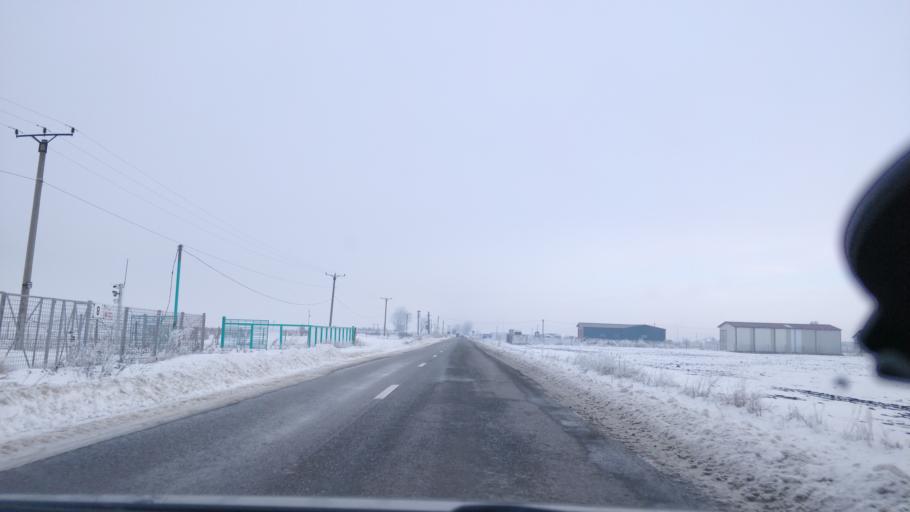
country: RO
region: Vrancea
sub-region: Comuna Vrancioaia
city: Focsani
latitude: 45.6978
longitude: 27.2230
